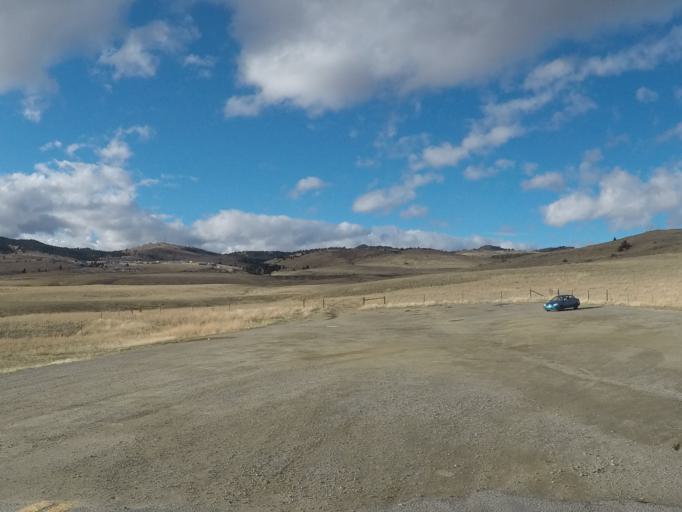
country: US
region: Montana
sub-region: Jefferson County
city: Boulder
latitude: 46.2472
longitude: -112.1197
